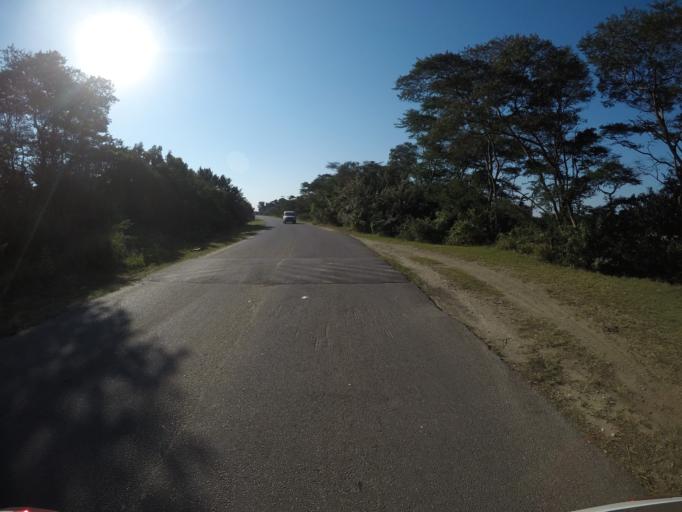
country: ZA
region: KwaZulu-Natal
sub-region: uThungulu District Municipality
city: Richards Bay
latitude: -28.7985
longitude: 32.0824
